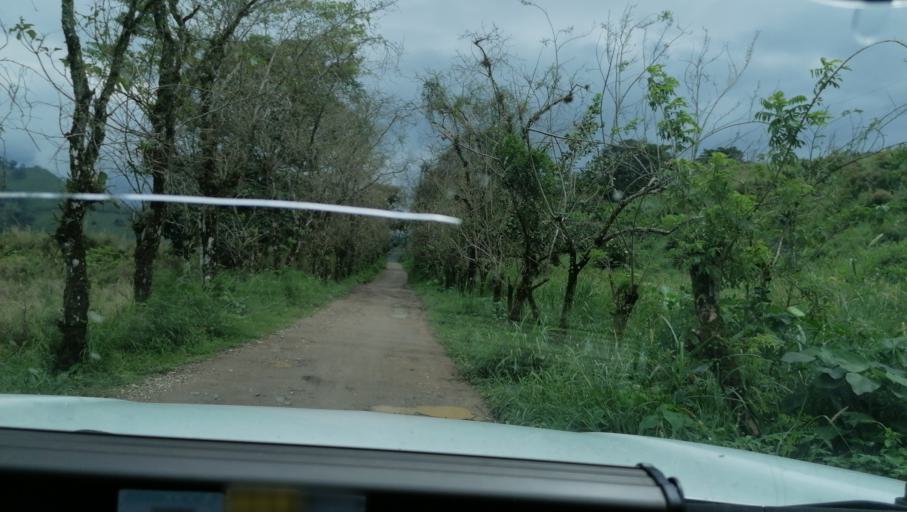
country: MX
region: Chiapas
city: Ixtacomitan
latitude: 17.3448
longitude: -93.1360
